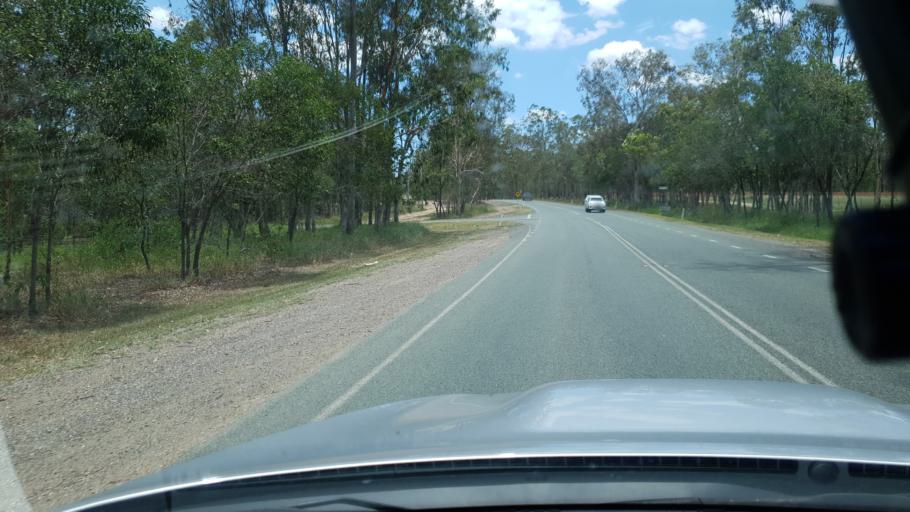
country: AU
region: Queensland
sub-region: Logan
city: North Maclean
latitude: -27.7347
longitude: 152.9849
